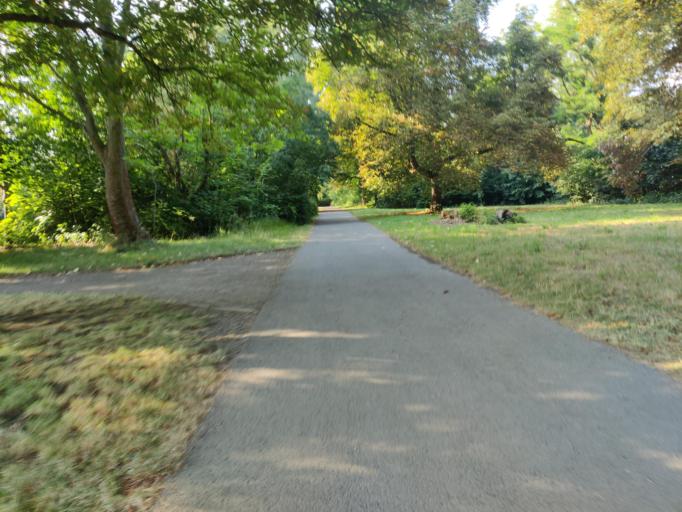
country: DE
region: Saxony
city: Bohlen
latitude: 51.2079
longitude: 12.3912
